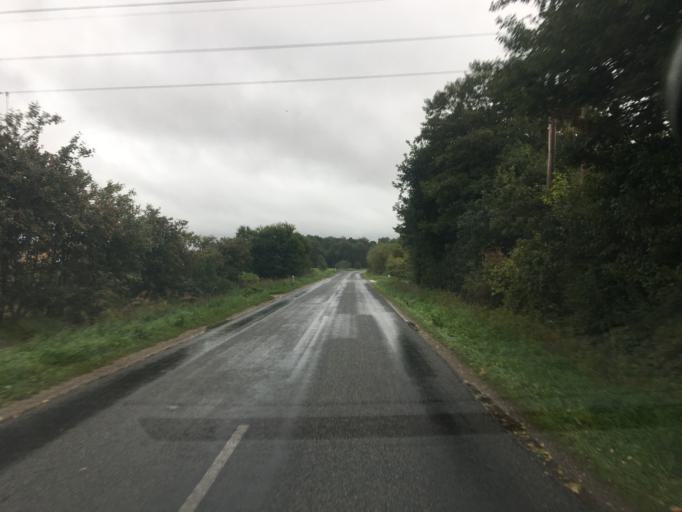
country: DE
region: Schleswig-Holstein
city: Bramstedtlund
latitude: 54.9609
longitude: 9.0517
